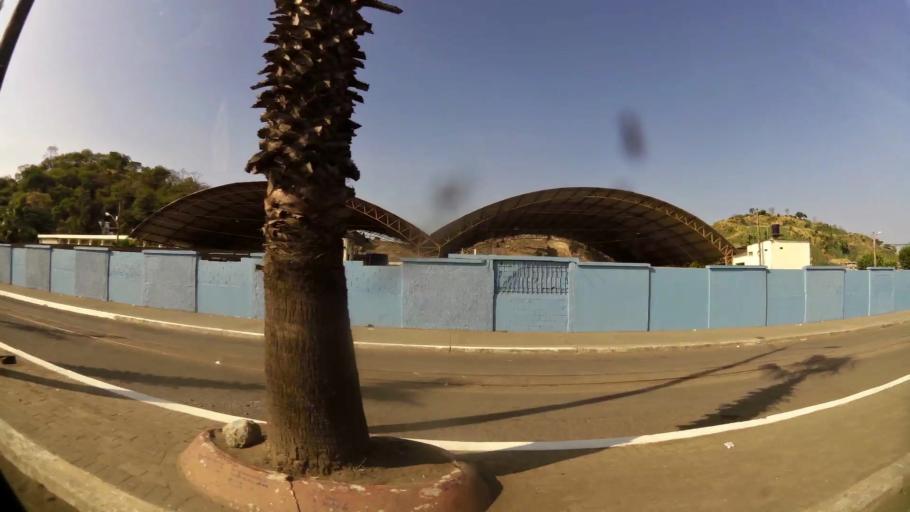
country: EC
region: Guayas
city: Eloy Alfaro
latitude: -2.1703
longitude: -79.8404
